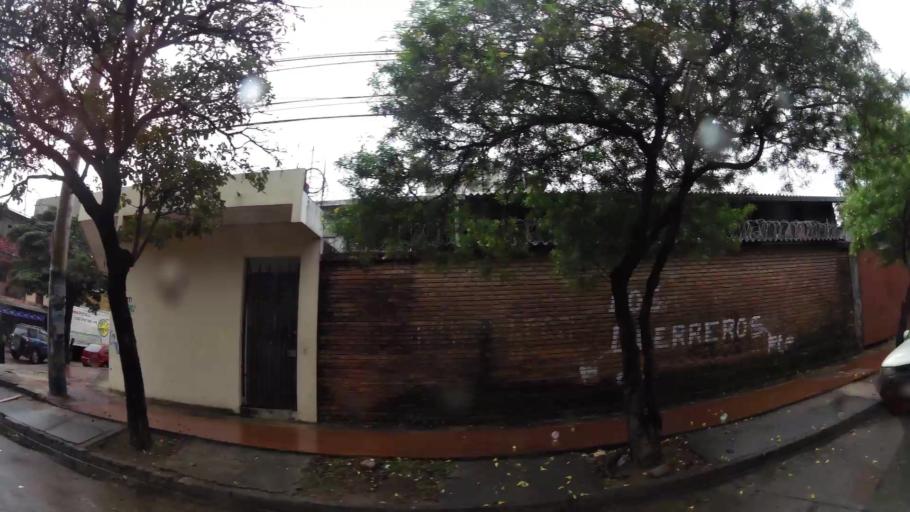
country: BO
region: Santa Cruz
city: Santa Cruz de la Sierra
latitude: -17.8056
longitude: -63.1872
